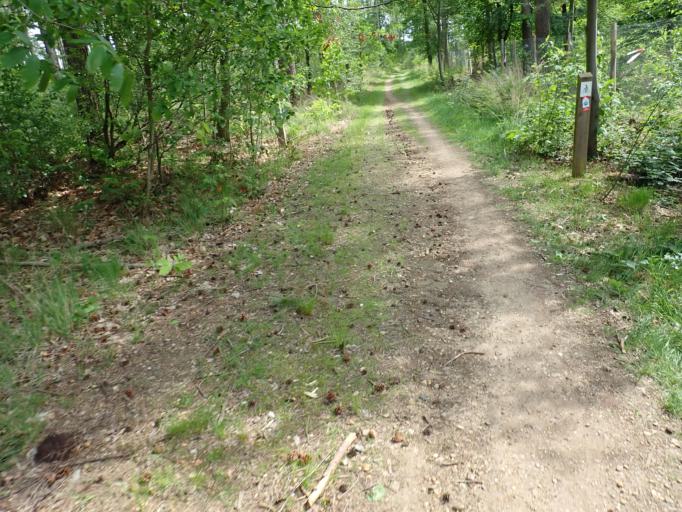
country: BE
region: Flanders
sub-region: Provincie Antwerpen
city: Westerlo
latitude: 51.0675
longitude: 4.9125
